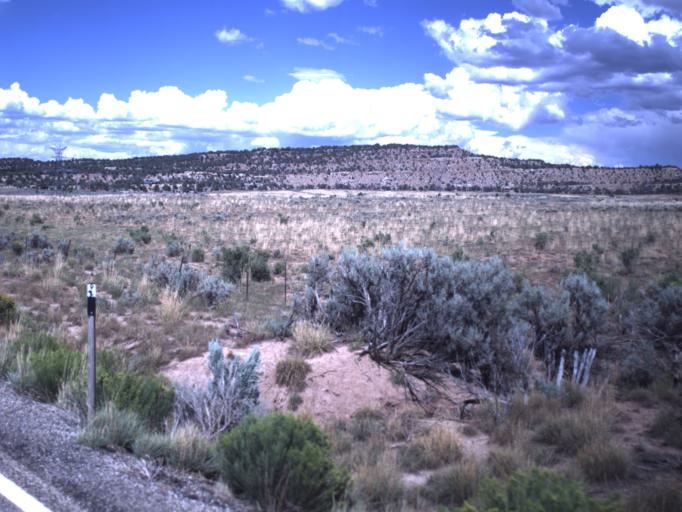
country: US
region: Utah
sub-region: Duchesne County
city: Duchesne
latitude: 40.2158
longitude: -110.7269
